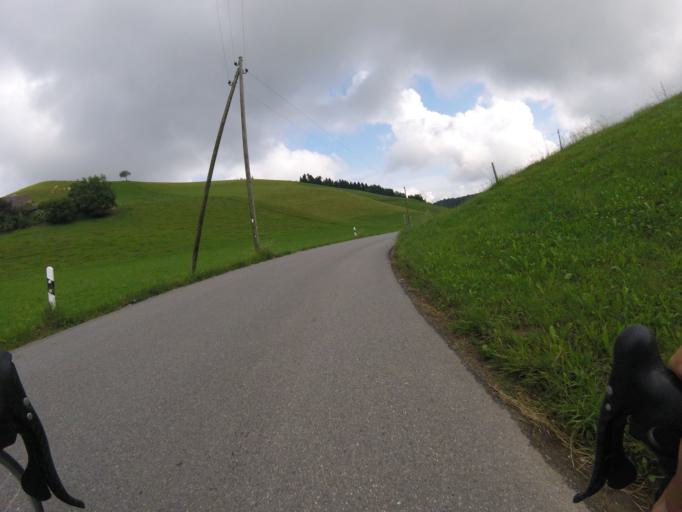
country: CH
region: Bern
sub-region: Emmental District
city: Krauchthal
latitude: 46.9770
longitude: 7.5793
